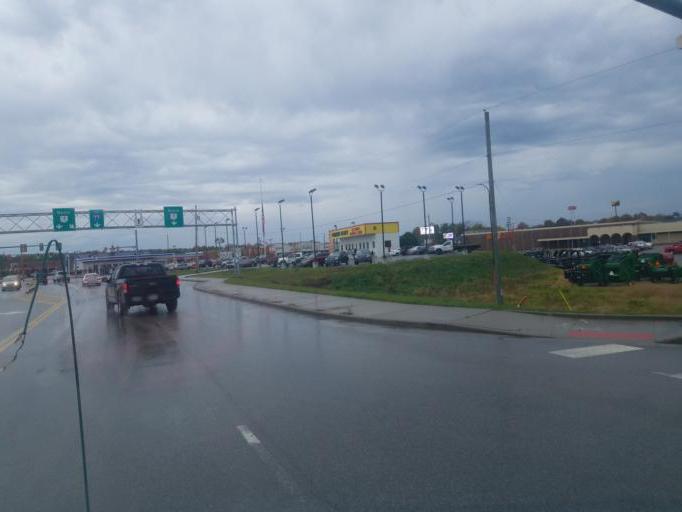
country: US
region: West Virginia
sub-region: Wood County
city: Williamstown
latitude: 39.4119
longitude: -81.4300
